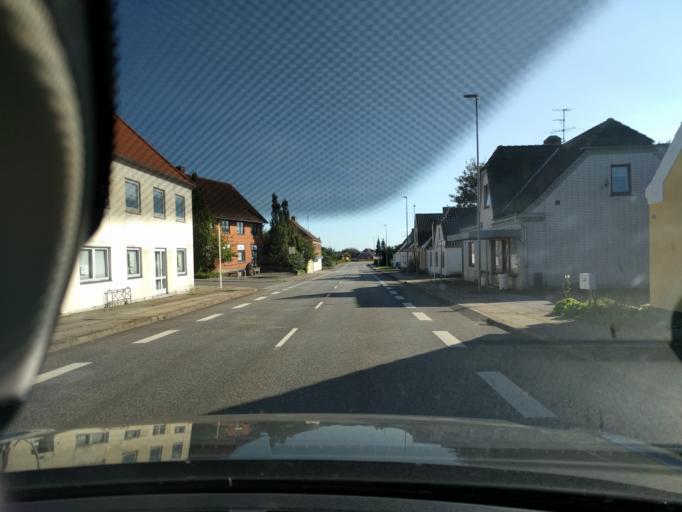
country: DK
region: North Denmark
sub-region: Vesthimmerland Kommune
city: Farso
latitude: 56.7904
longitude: 9.2159
